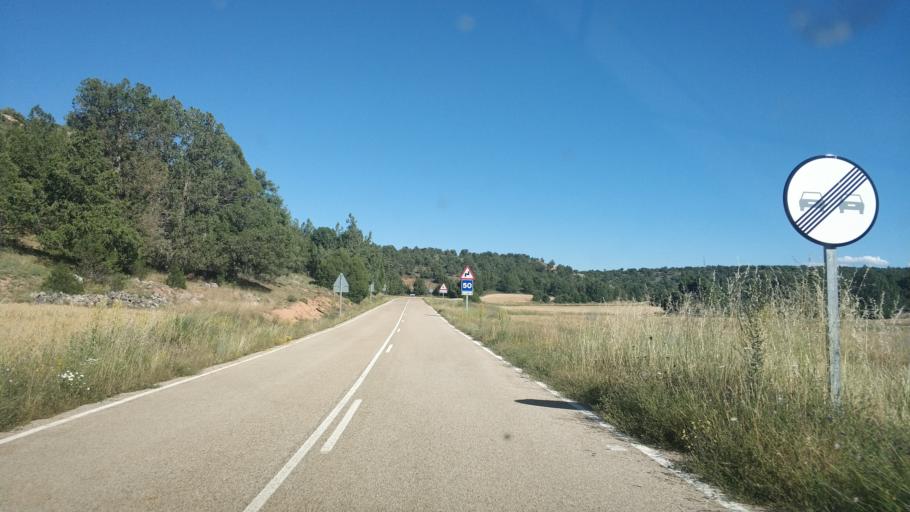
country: ES
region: Castille and Leon
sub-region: Provincia de Soria
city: Liceras
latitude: 41.4384
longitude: -3.2137
